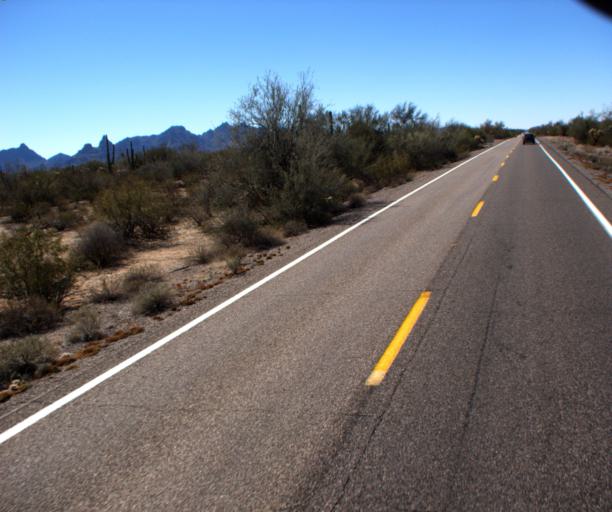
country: US
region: Arizona
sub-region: Pima County
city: Ajo
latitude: 32.1886
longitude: -112.7608
